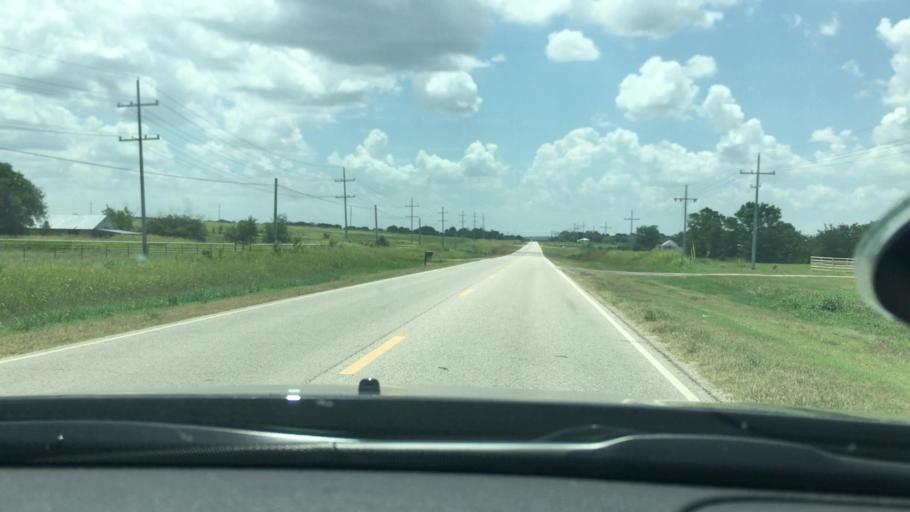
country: US
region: Oklahoma
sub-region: Pontotoc County
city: Ada
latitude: 34.6408
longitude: -96.6349
